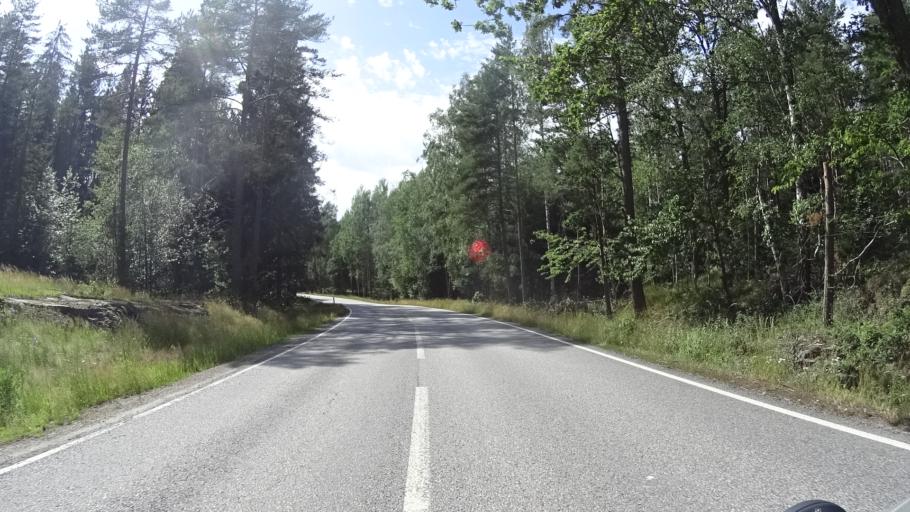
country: SE
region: Kalmar
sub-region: Vasterviks Kommun
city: Overum
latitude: 58.0799
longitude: 16.1793
